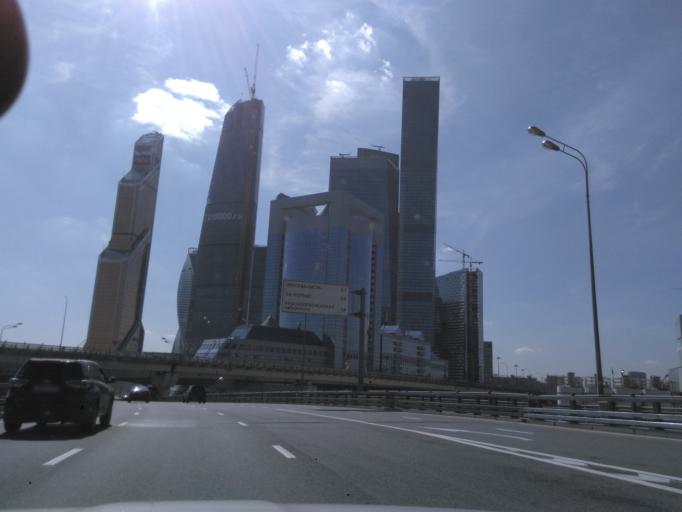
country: RU
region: Moskovskaya
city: Presnenskiy
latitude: 55.7541
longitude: 37.5295
